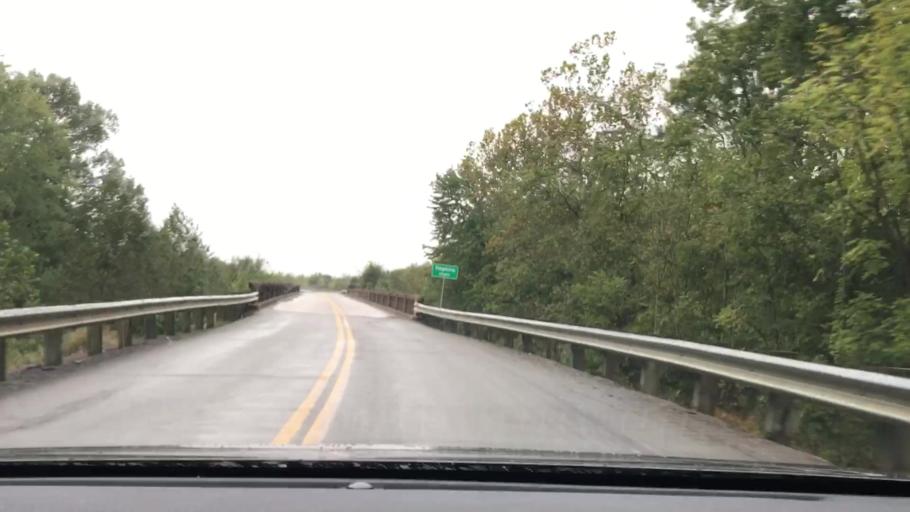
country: US
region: Kentucky
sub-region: McLean County
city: Calhoun
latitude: 37.3951
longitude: -87.3047
